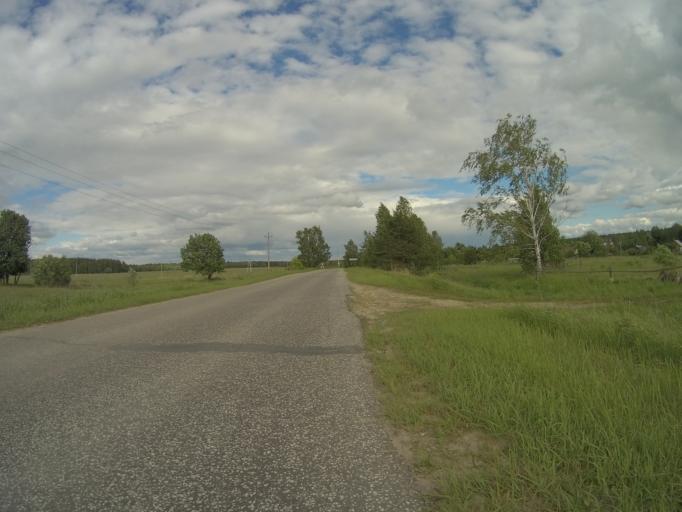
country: RU
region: Vladimir
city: Bogolyubovo
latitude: 56.1138
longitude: 40.5306
